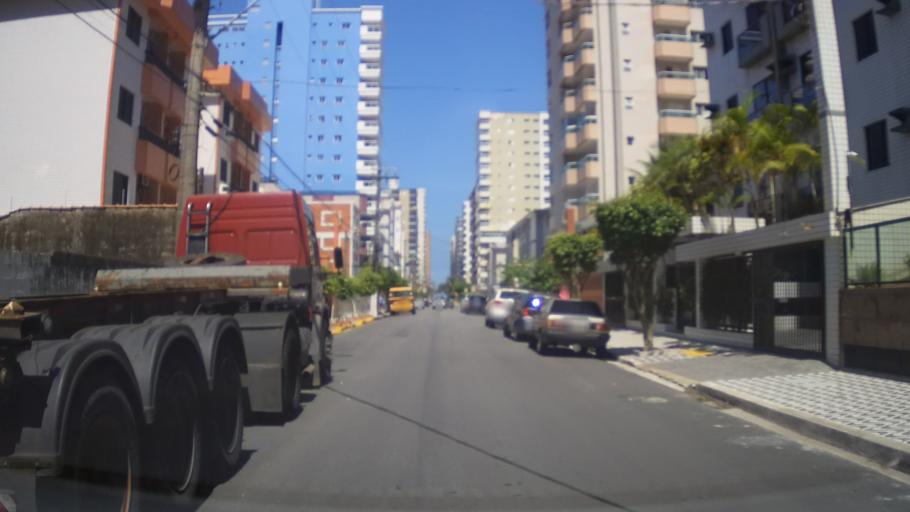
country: BR
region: Sao Paulo
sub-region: Praia Grande
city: Praia Grande
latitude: -24.0090
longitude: -46.4058
